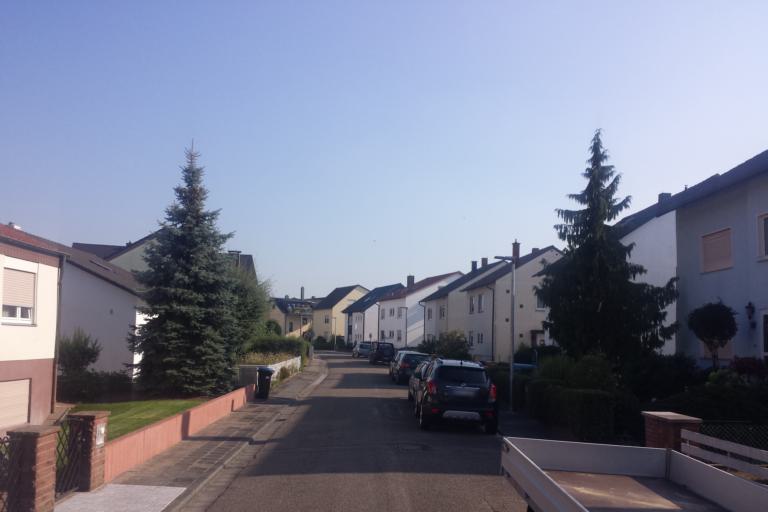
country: DE
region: Rheinland-Pfalz
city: Waldsee
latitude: 49.3909
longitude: 8.4339
